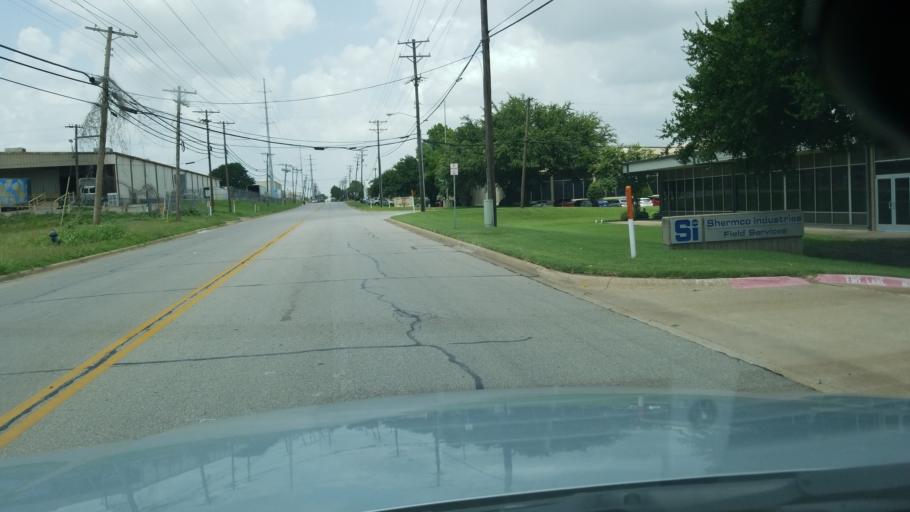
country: US
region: Texas
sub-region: Dallas County
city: Irving
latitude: 32.8179
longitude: -96.9168
